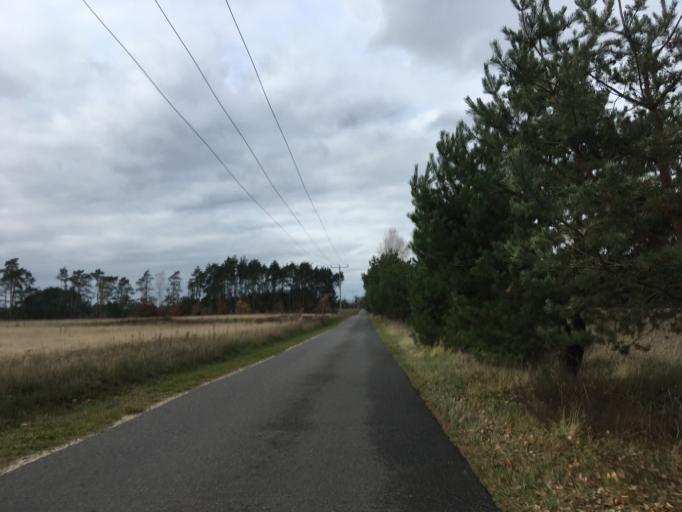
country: DE
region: Brandenburg
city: Jamlitz
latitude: 52.0830
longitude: 14.4462
